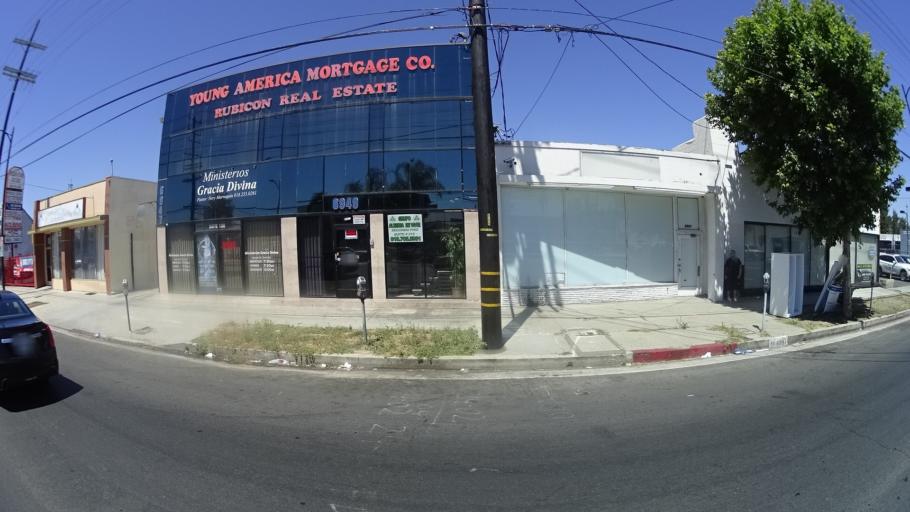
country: US
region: California
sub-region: Los Angeles County
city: Northridge
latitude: 34.1972
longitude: -118.5361
